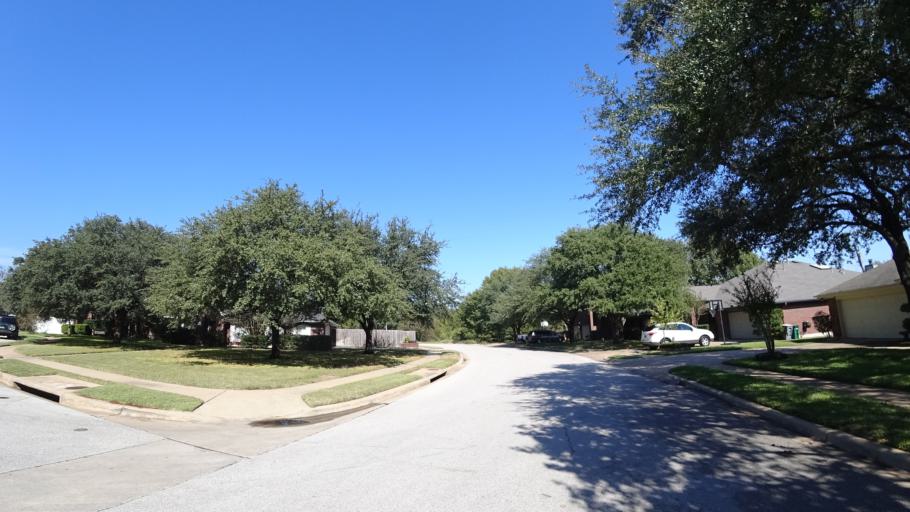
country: US
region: Texas
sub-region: Travis County
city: Shady Hollow
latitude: 30.2170
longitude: -97.8565
